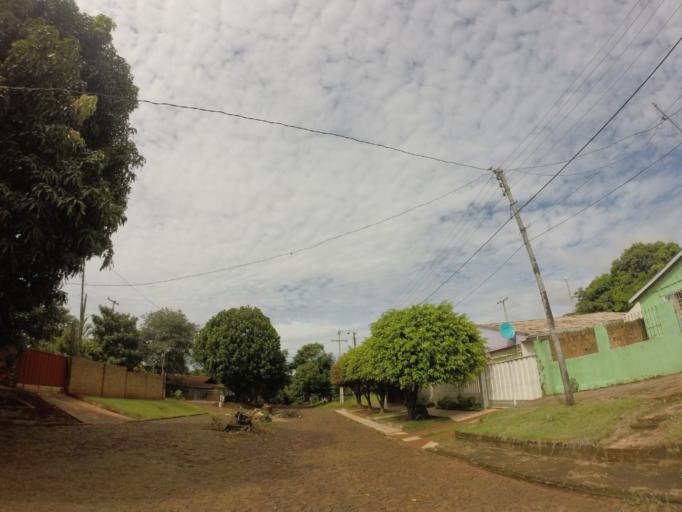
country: PY
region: Alto Parana
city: Ciudad del Este
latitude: -25.4093
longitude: -54.6455
